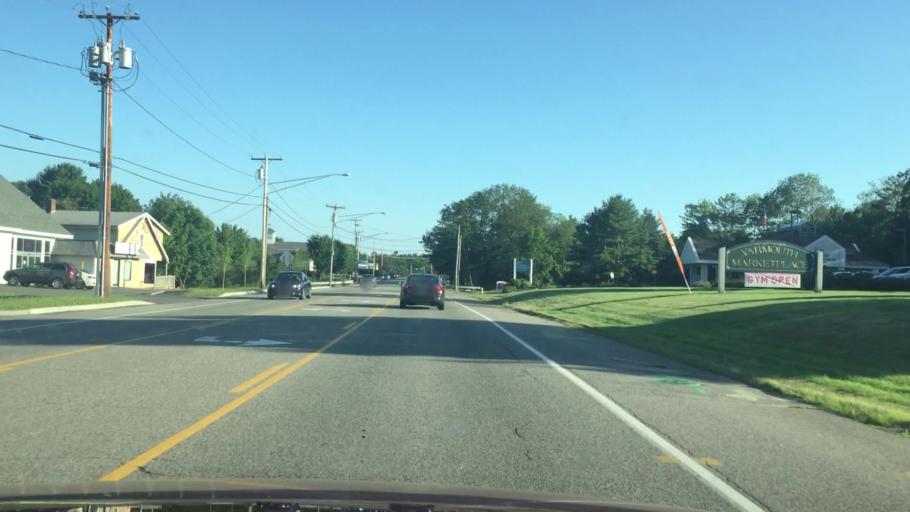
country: US
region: Maine
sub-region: Cumberland County
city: Yarmouth
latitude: 43.7970
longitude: -70.1885
